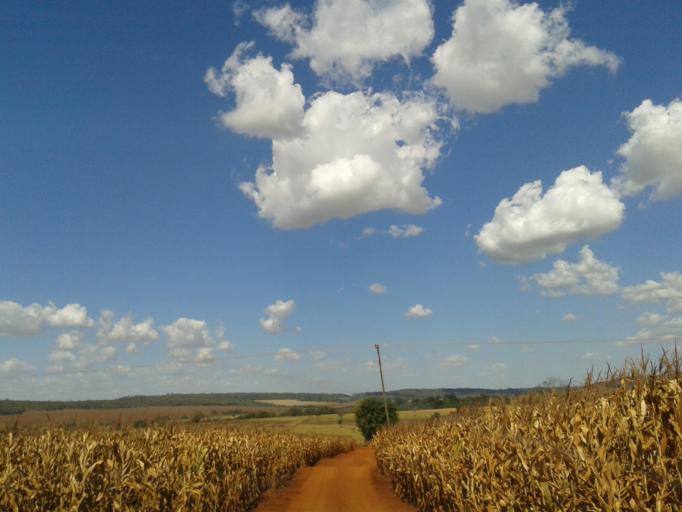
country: BR
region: Minas Gerais
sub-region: Capinopolis
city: Capinopolis
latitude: -18.6246
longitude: -49.4731
